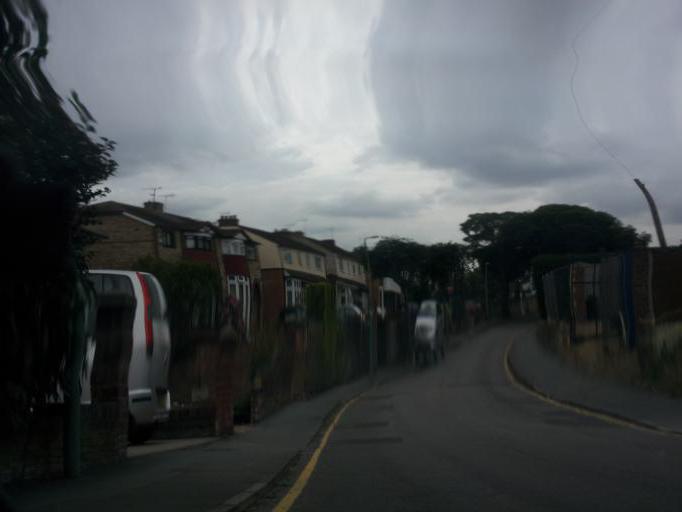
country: GB
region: England
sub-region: Kent
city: Rainham
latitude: 51.3685
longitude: 0.6055
